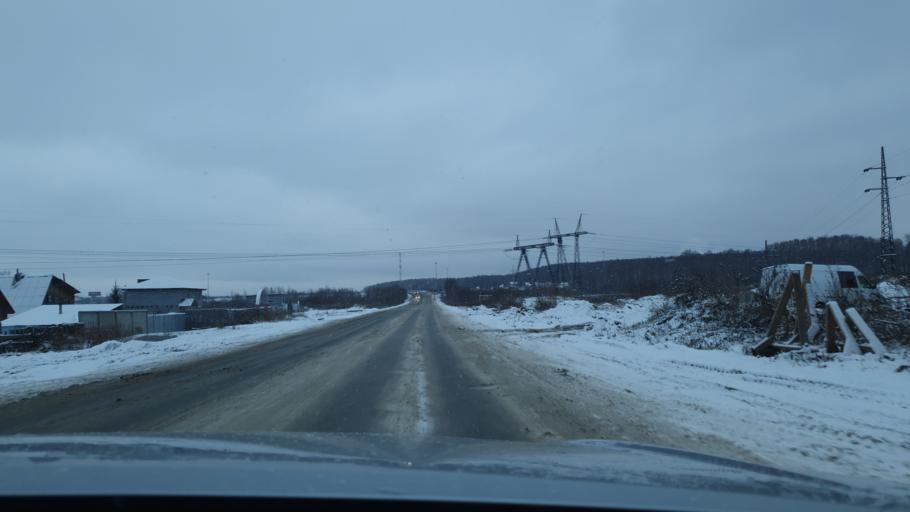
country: RU
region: Sverdlovsk
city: Istok
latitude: 56.7747
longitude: 60.7385
